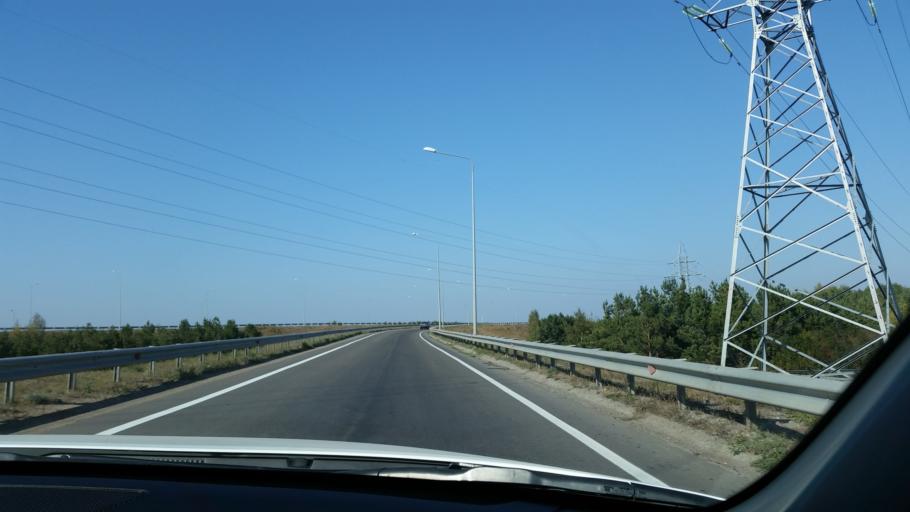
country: KZ
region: Astana Qalasy
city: Astana
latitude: 51.2015
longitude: 71.3103
